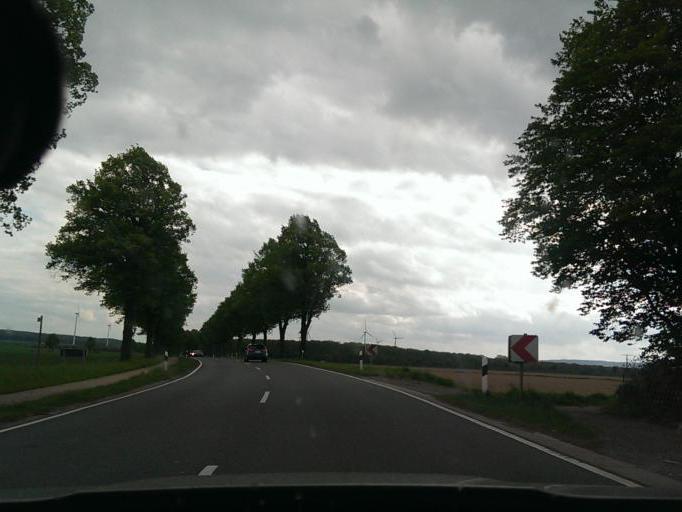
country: DE
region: Lower Saxony
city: Pattensen
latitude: 52.2147
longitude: 9.7466
